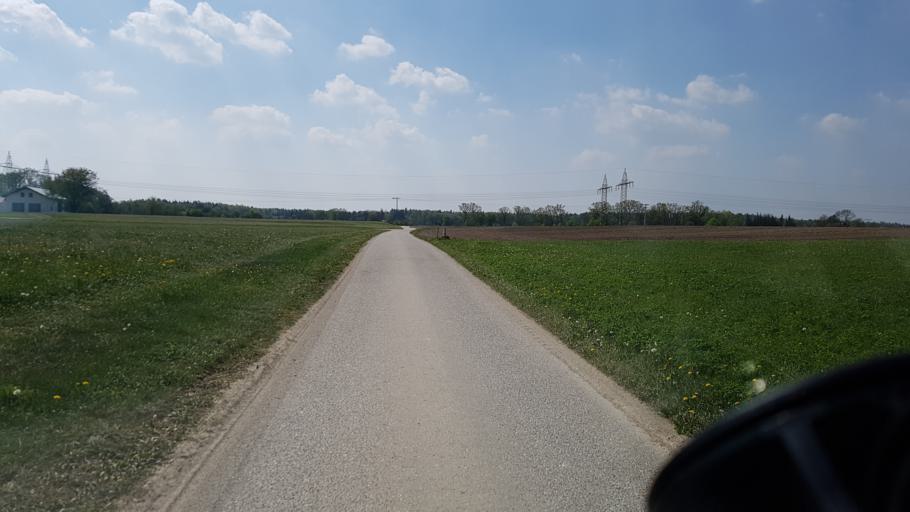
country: DE
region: Bavaria
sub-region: Upper Bavaria
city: Perach
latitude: 48.2544
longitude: 12.8024
